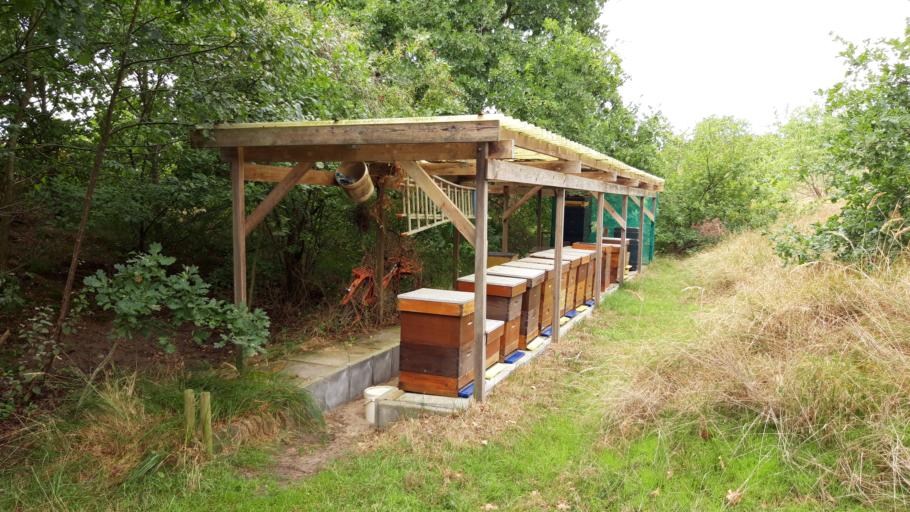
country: NL
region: Friesland
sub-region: Gemeente Schiermonnikoog
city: Schiermonnikoog
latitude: 53.4832
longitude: 6.1776
